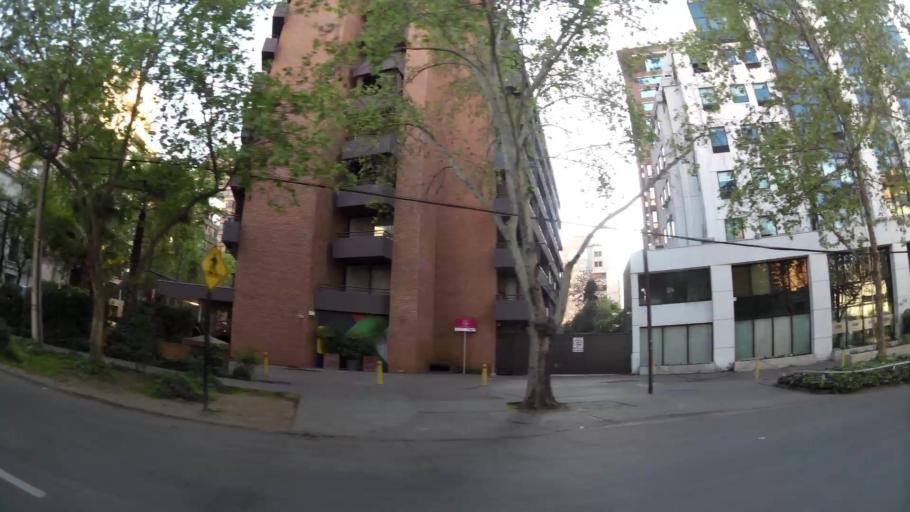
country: CL
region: Santiago Metropolitan
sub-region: Provincia de Santiago
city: Villa Presidente Frei, Nunoa, Santiago, Chile
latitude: -33.4166
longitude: -70.6021
